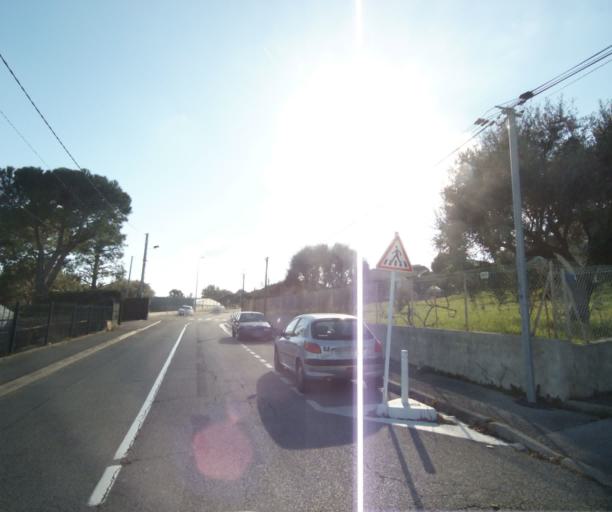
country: FR
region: Provence-Alpes-Cote d'Azur
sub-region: Departement des Alpes-Maritimes
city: Biot
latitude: 43.6011
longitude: 7.1087
